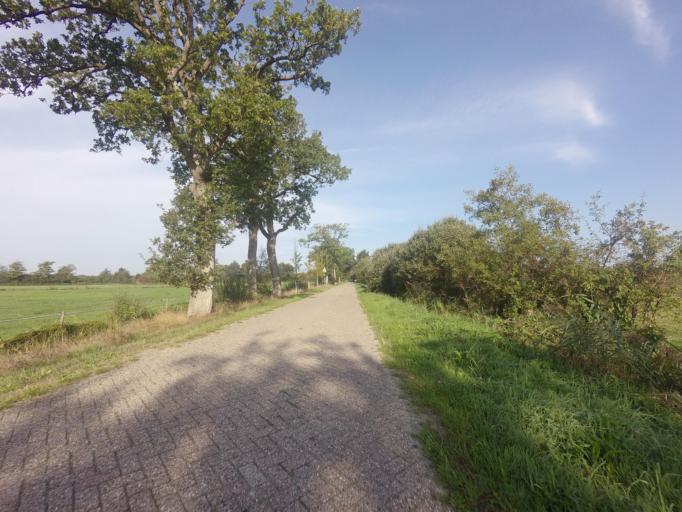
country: NL
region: Groningen
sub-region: Gemeente Leek
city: Leek
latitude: 53.1479
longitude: 6.4716
